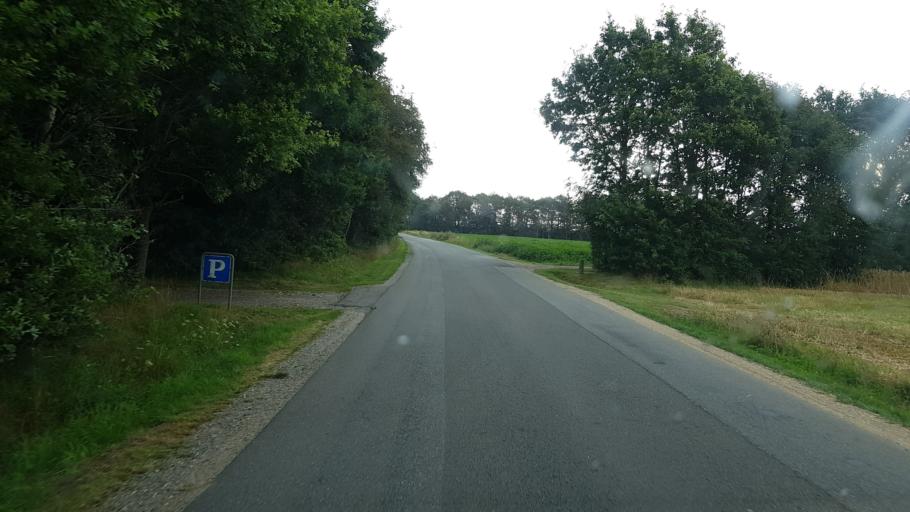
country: DK
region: South Denmark
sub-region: Billund Kommune
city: Grindsted
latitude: 55.6391
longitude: 8.8295
